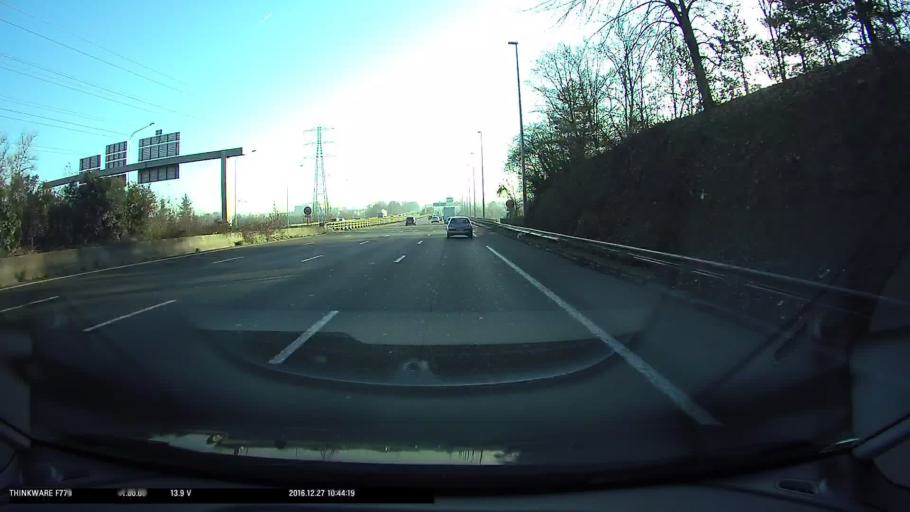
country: FR
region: Ile-de-France
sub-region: Departement du Val-d'Oise
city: Pontoise
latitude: 49.0365
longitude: 2.0934
